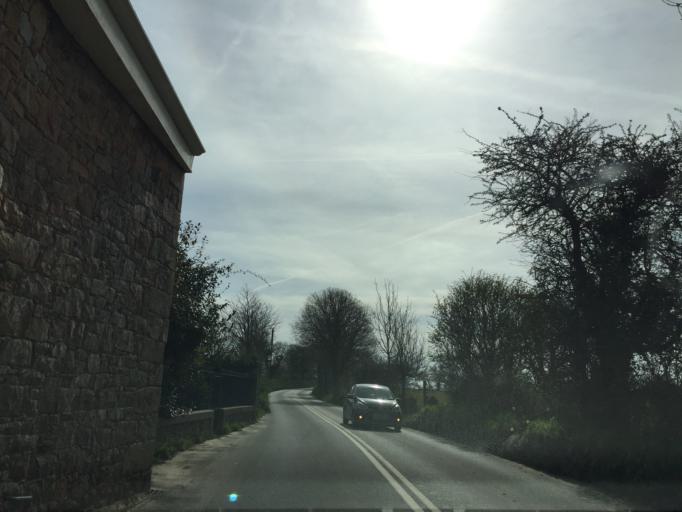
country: JE
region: St Helier
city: Saint Helier
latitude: 49.2217
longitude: -2.0621
